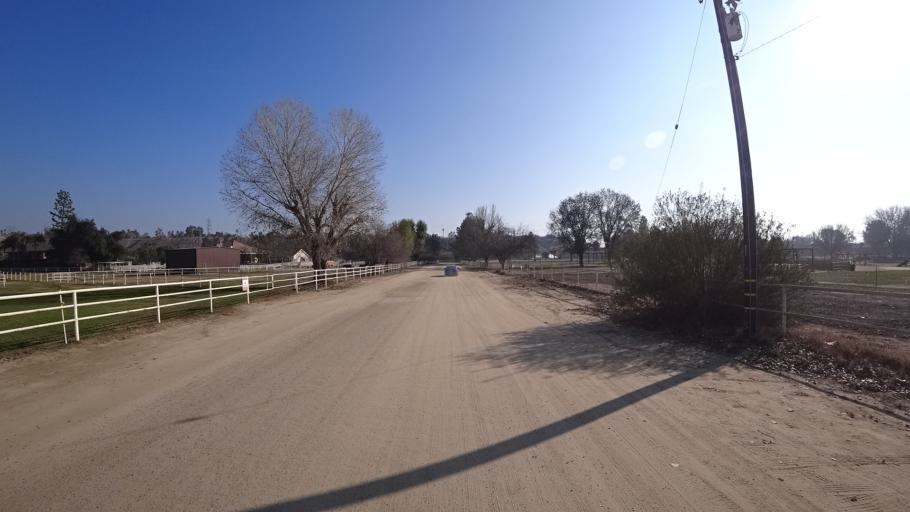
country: US
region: California
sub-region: Kern County
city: Oildale
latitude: 35.4074
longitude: -119.0055
